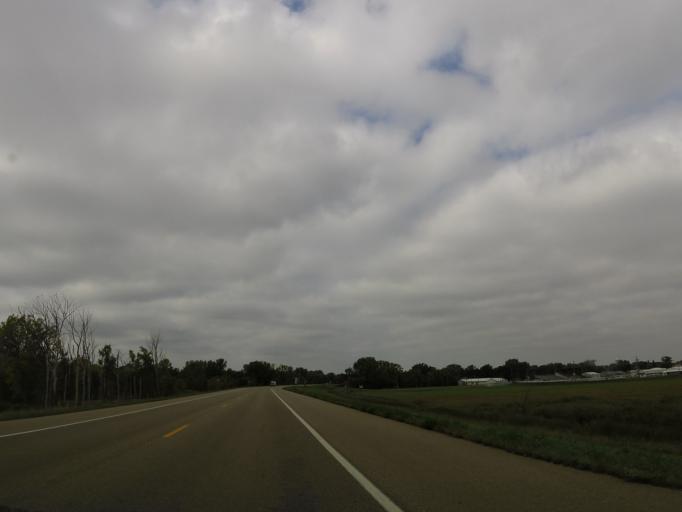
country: US
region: Minnesota
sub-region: Chippewa County
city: Montevideo
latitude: 44.9319
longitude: -95.7181
